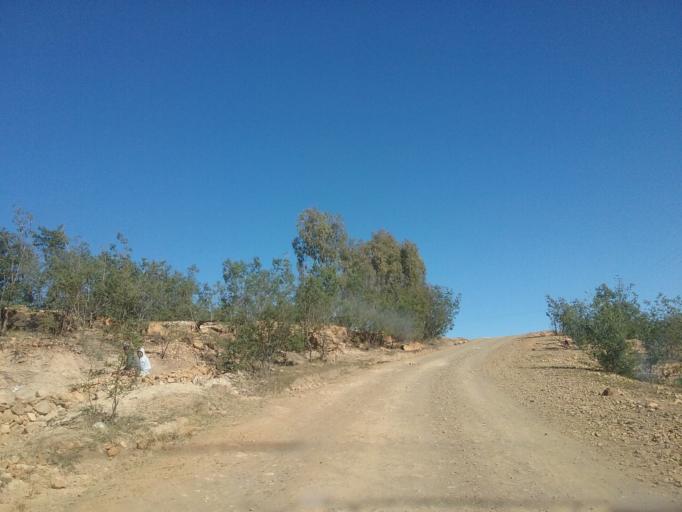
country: LS
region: Maseru
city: Maseru
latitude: -29.4499
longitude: 27.5789
